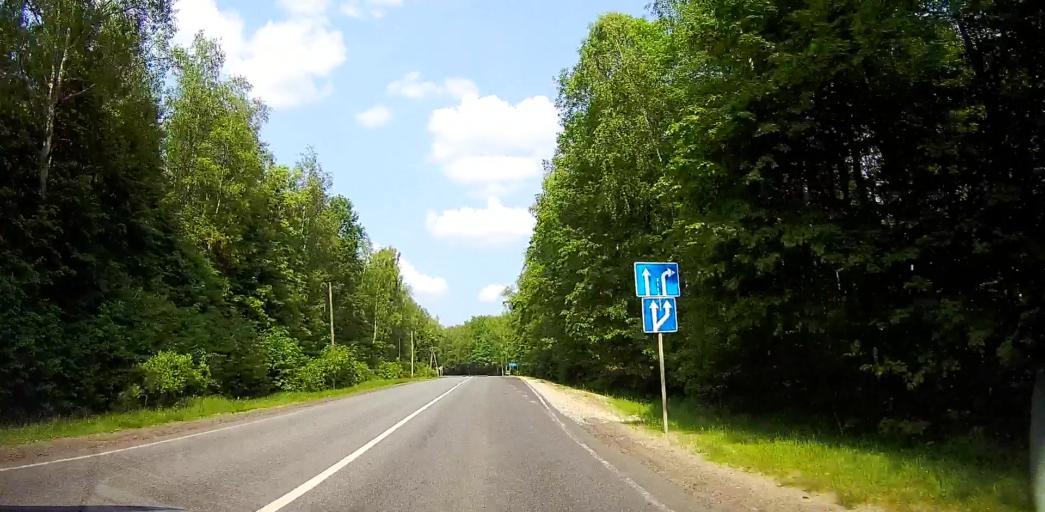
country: RU
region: Moskovskaya
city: Stupino
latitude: 54.9792
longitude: 38.1635
